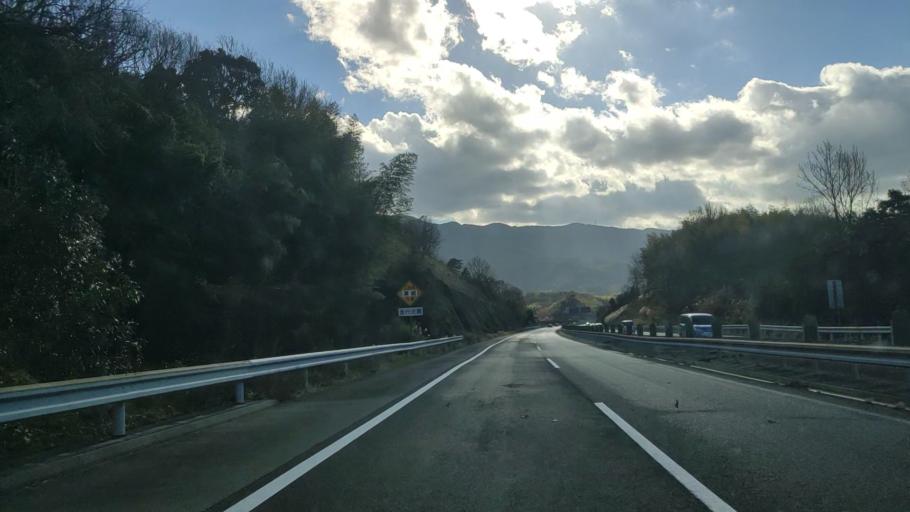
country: JP
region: Ehime
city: Kawanoecho
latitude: 33.9952
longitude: 133.5957
